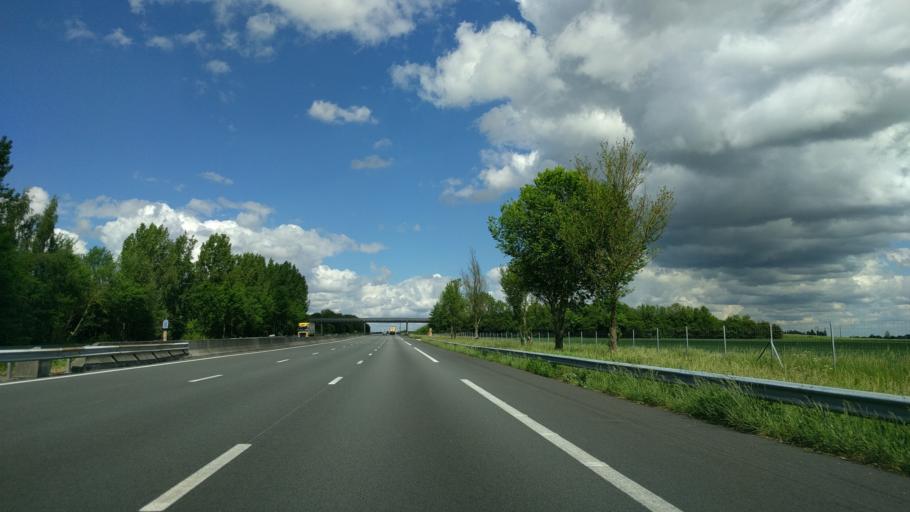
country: FR
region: Picardie
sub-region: Departement de la Somme
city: Chaulnes
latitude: 49.8108
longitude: 2.8178
